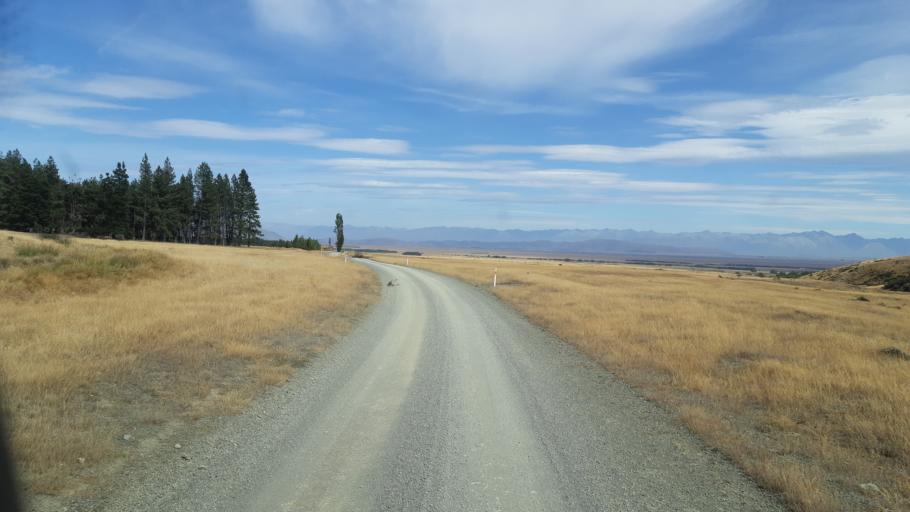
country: NZ
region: Canterbury
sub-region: Timaru District
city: Pleasant Point
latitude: -44.1935
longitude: 170.5707
